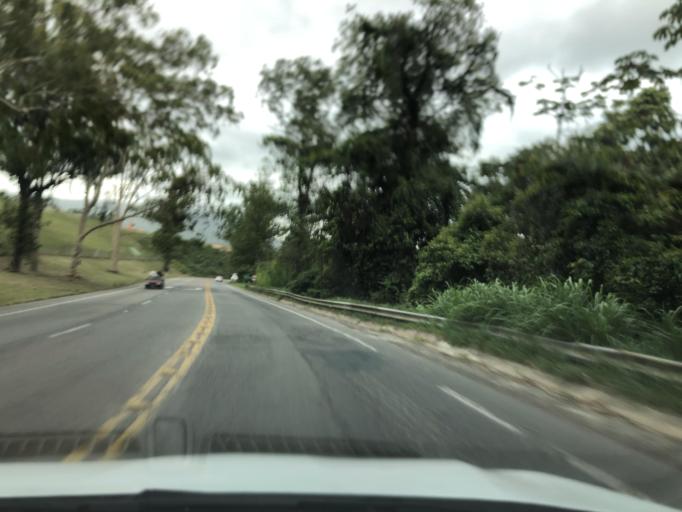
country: BR
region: Santa Catarina
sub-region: Ibirama
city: Ibirama
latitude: -27.1055
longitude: -49.5220
